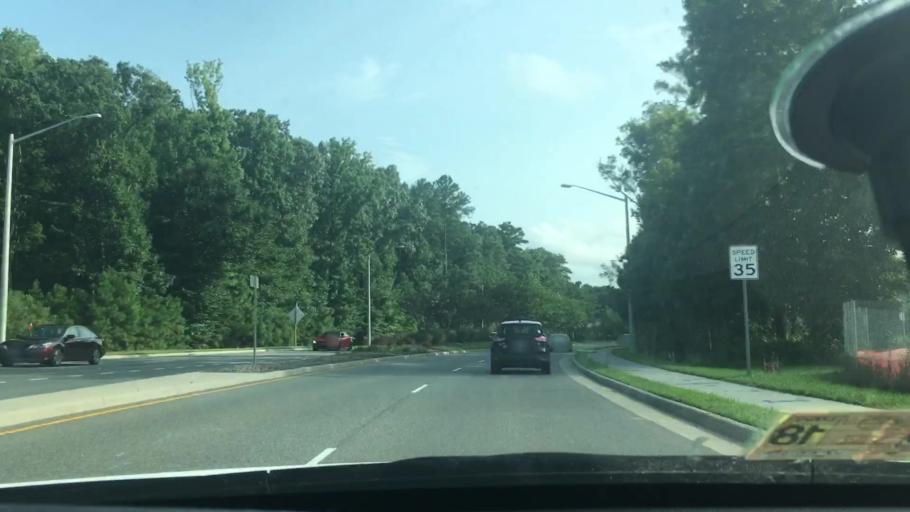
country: US
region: Virginia
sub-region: City of Virginia Beach
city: Virginia Beach
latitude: 36.8280
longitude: -75.9972
